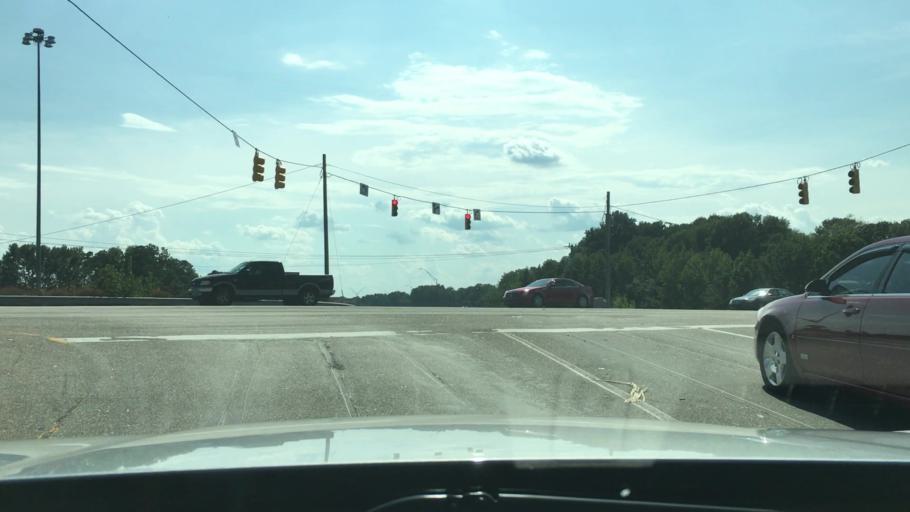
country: US
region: North Carolina
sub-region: Robeson County
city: Lumberton
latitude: 34.6236
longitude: -79.0526
